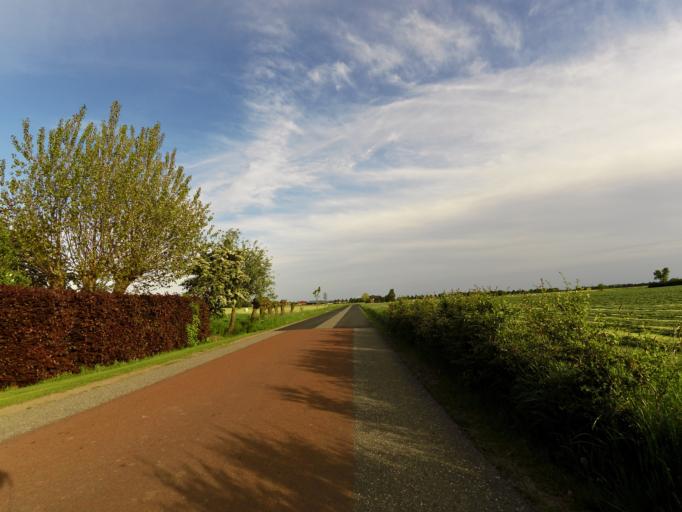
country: NL
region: Gelderland
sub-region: Gemeente Montferland
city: s-Heerenberg
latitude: 51.9079
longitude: 6.2985
